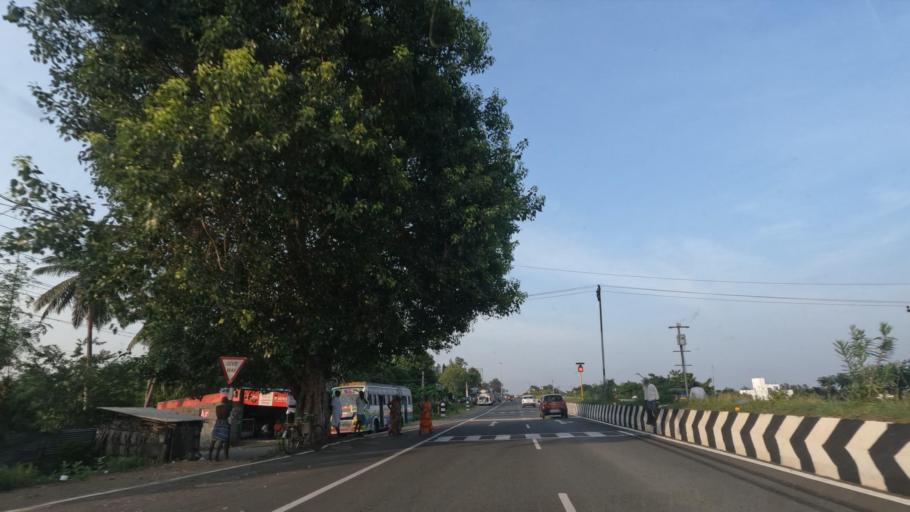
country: IN
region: Tamil Nadu
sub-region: Kancheepuram
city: Mamallapuram
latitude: 12.6890
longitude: 80.2171
